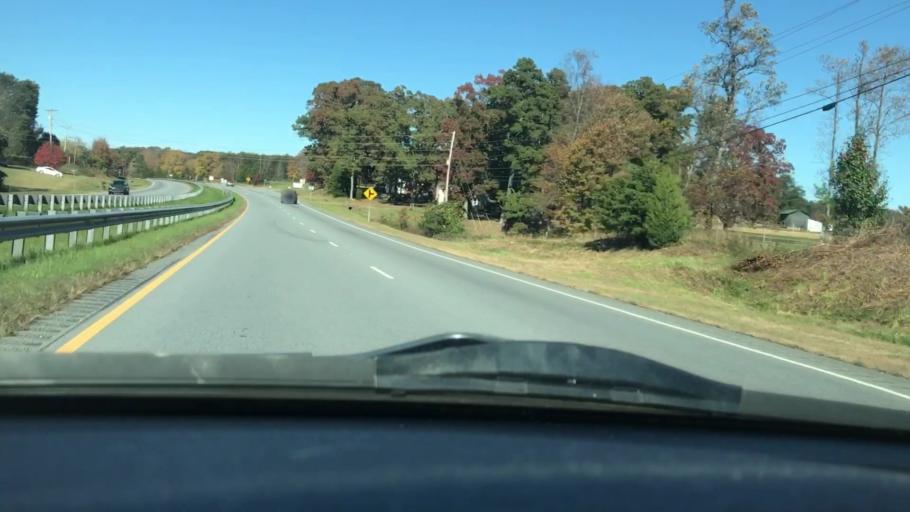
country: US
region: North Carolina
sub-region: Rockingham County
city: Madison
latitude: 36.3366
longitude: -79.9443
